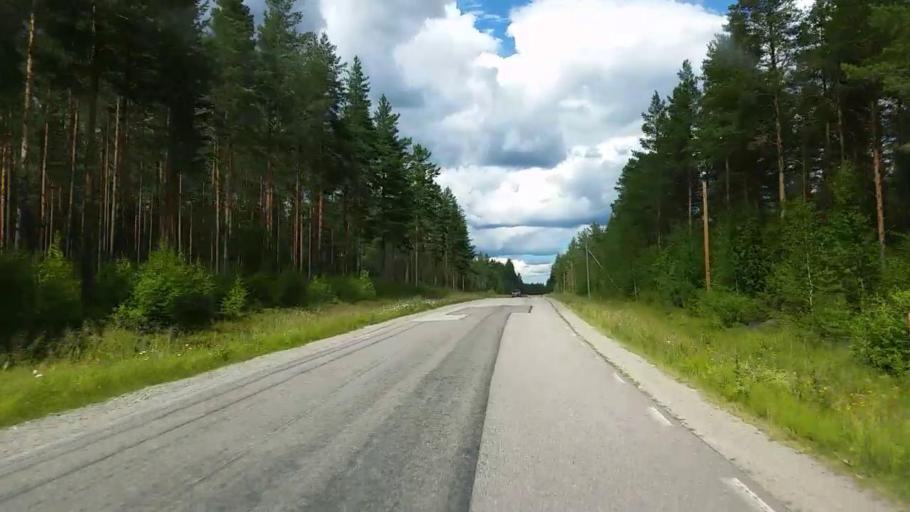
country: SE
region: Gaevleborg
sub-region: Ovanakers Kommun
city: Edsbyn
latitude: 61.4019
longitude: 15.8961
